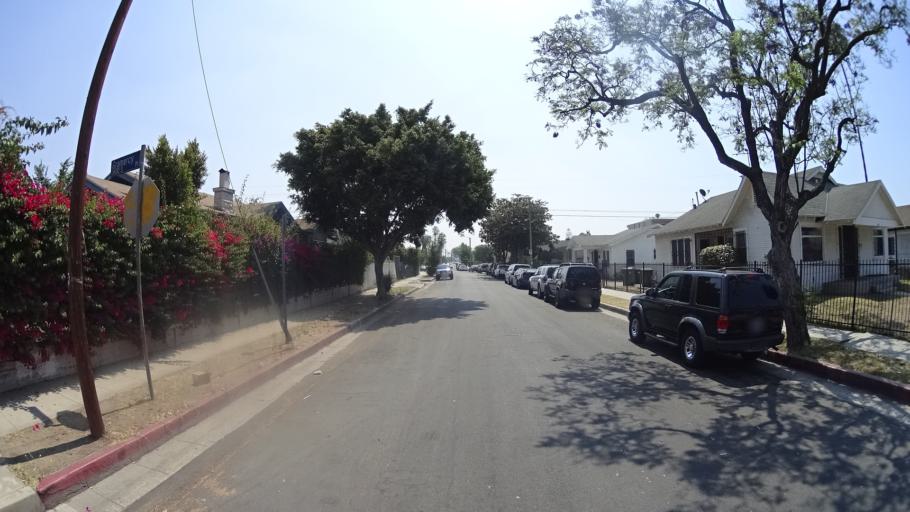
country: US
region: California
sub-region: Los Angeles County
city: View Park-Windsor Hills
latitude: 34.0246
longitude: -118.3137
